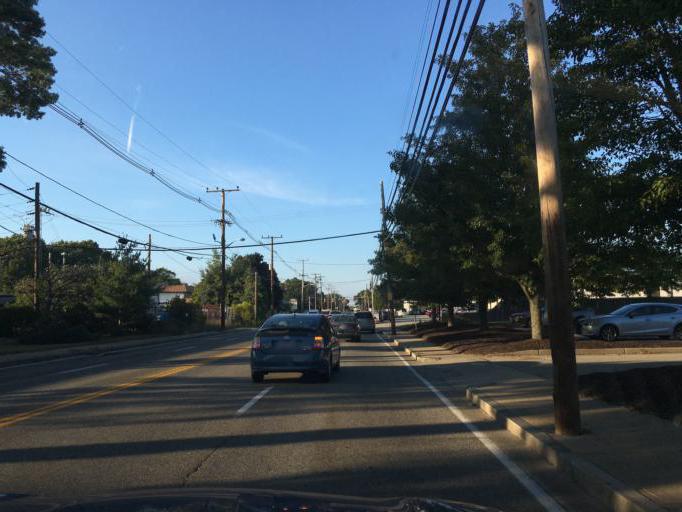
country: US
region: Rhode Island
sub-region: Kent County
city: Warwick
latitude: 41.7356
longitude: -71.4405
